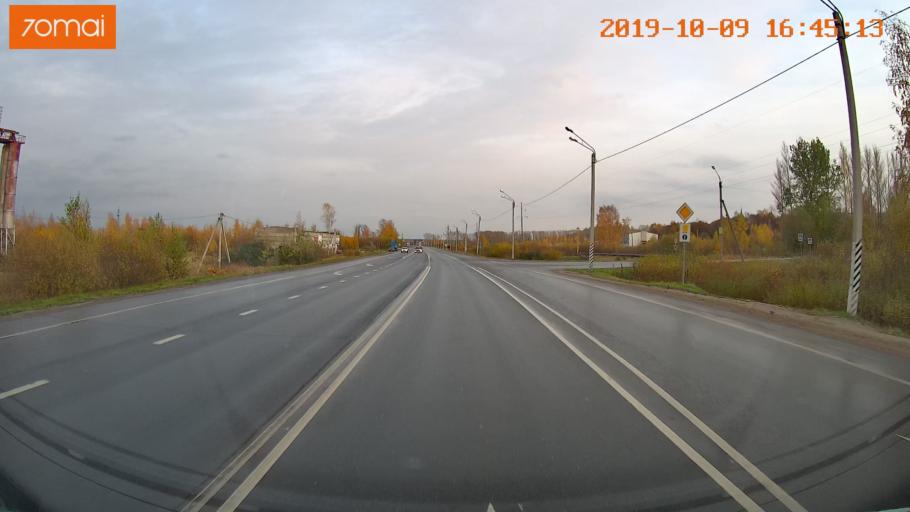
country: RU
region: Kostroma
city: Volgorechensk
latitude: 57.4475
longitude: 41.1516
